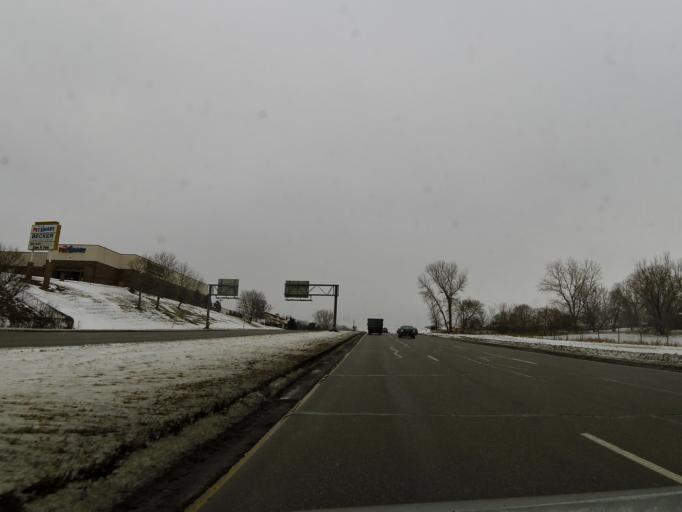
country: US
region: Minnesota
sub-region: Dakota County
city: Burnsville
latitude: 44.7429
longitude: -93.2764
